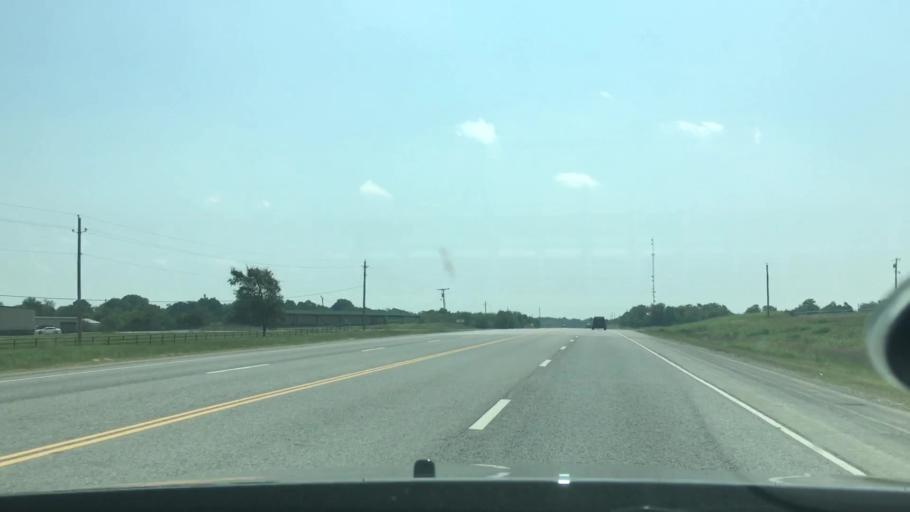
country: US
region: Oklahoma
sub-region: Atoka County
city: Atoka
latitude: 34.3639
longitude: -96.0992
